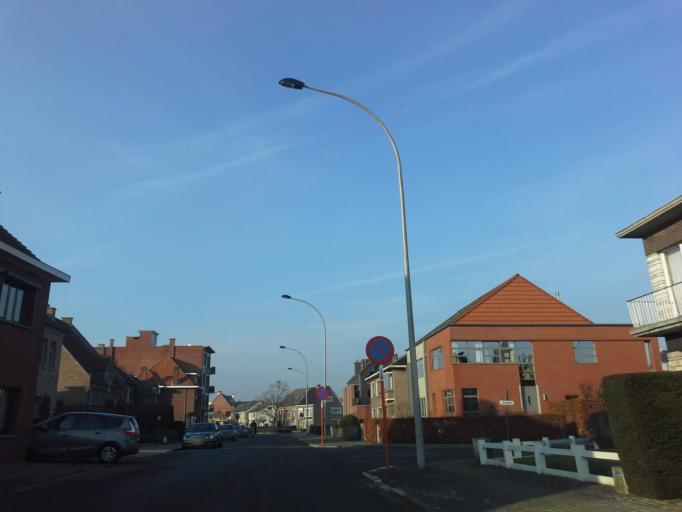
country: BE
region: Flanders
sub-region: Provincie Antwerpen
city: Geel
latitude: 51.1553
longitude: 4.9900
